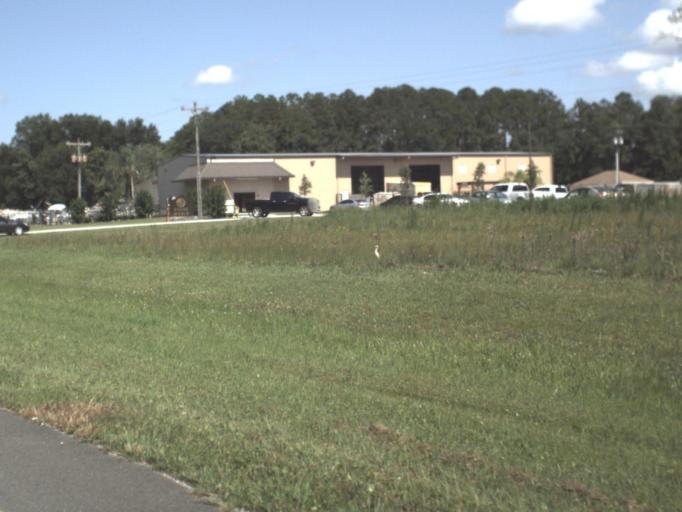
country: US
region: Florida
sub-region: Clay County
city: Green Cove Springs
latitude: 29.9848
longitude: -81.6667
